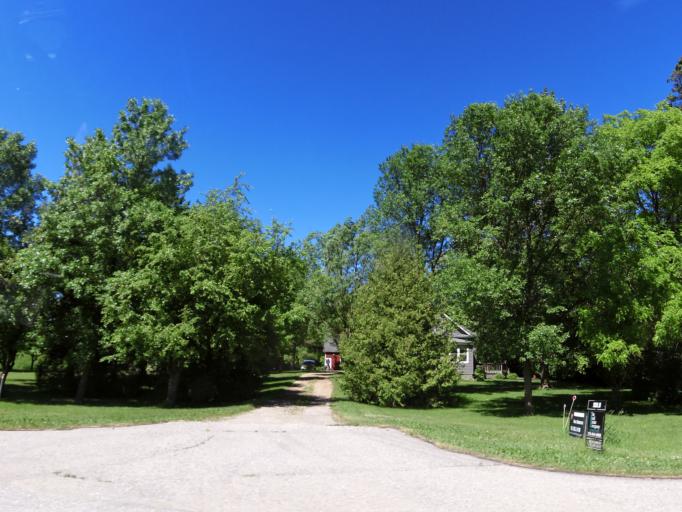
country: US
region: Minnesota
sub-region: Mahnomen County
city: Mahnomen
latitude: 47.5413
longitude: -95.9822
